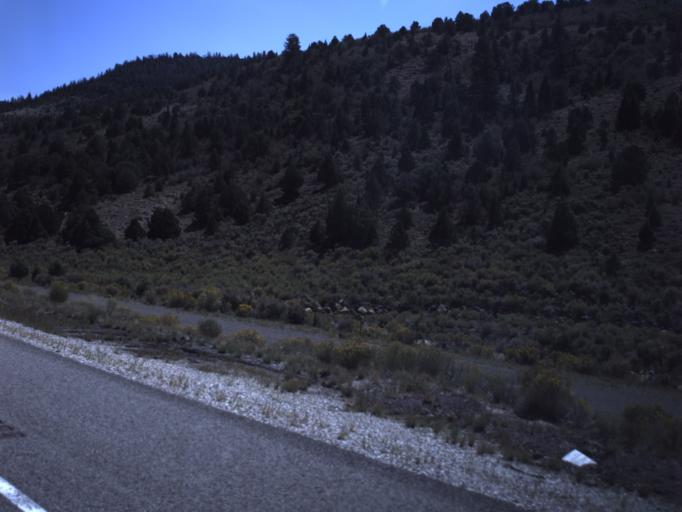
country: US
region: Utah
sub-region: Wayne County
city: Loa
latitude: 38.7621
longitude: -111.4610
